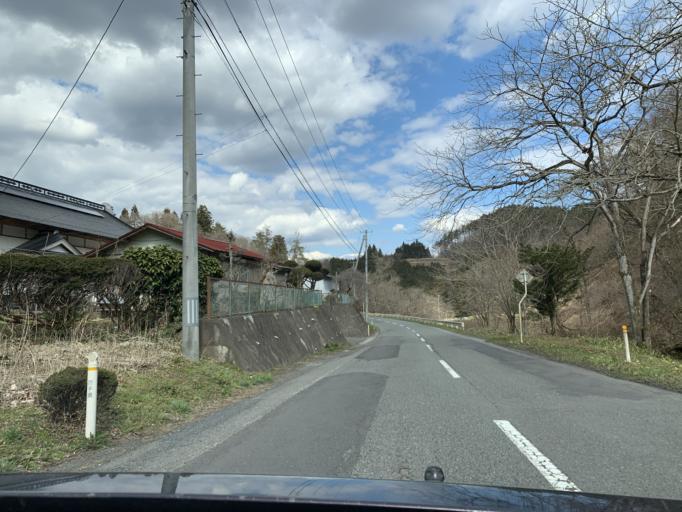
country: JP
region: Iwate
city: Ichinoseki
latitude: 38.8285
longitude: 141.3337
